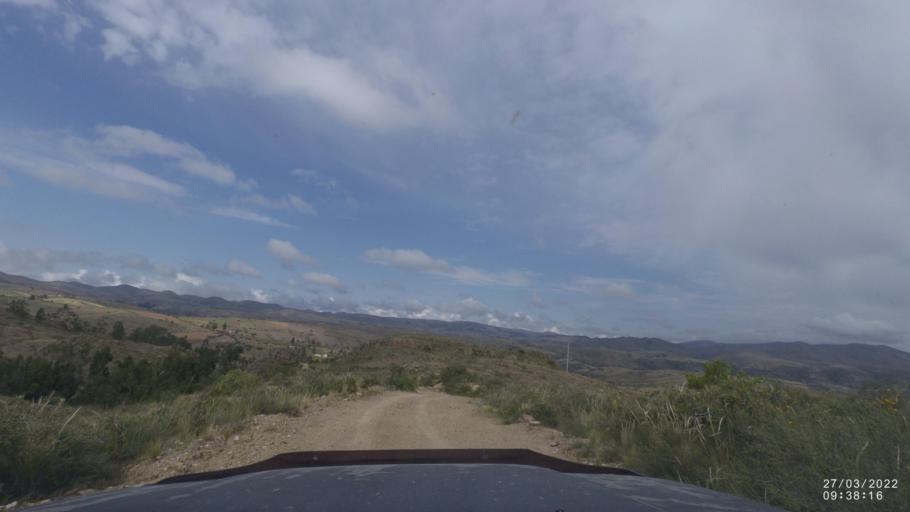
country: BO
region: Cochabamba
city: Cliza
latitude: -17.7469
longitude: -65.8946
